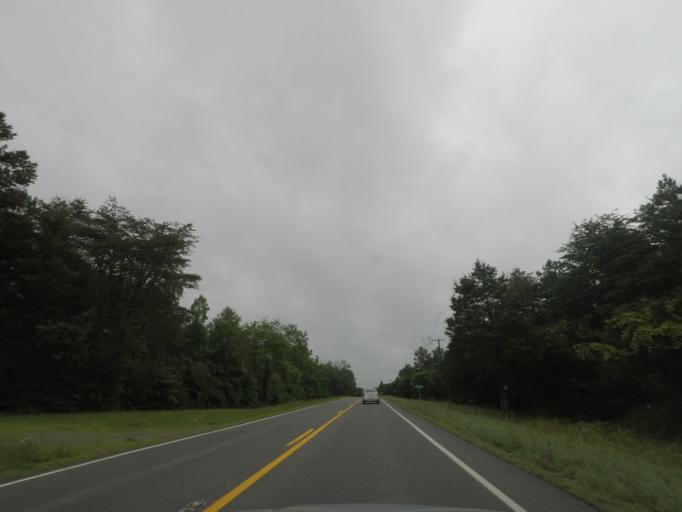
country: US
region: Virginia
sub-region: Fluvanna County
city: Palmyra
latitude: 37.8435
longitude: -78.2725
